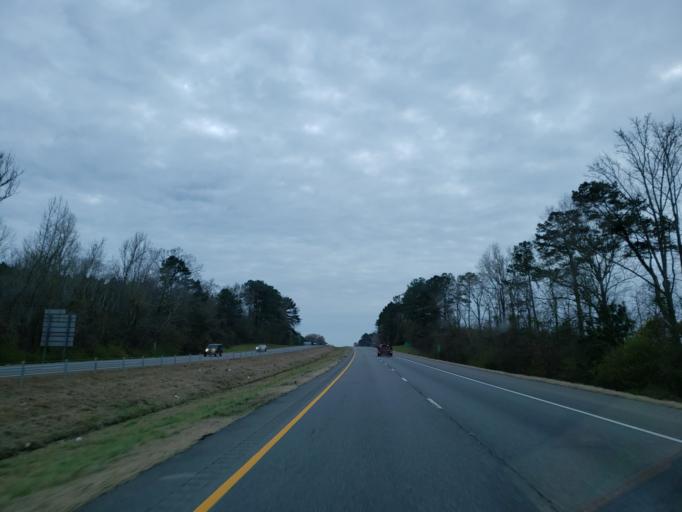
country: US
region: Alabama
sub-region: Greene County
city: Eutaw
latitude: 32.8626
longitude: -87.9336
